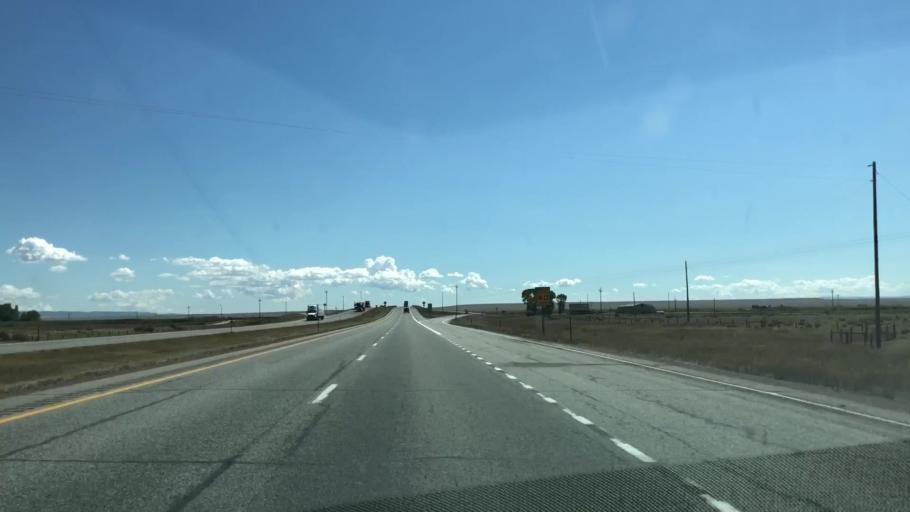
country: US
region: Wyoming
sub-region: Albany County
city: Laramie
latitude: 41.3999
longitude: -105.8284
